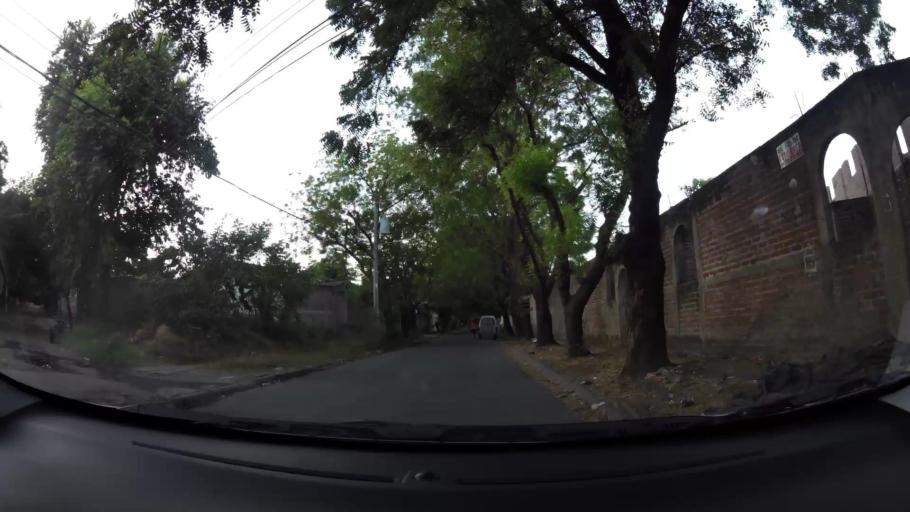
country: SV
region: San Miguel
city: San Miguel
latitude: 13.4814
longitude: -88.1582
